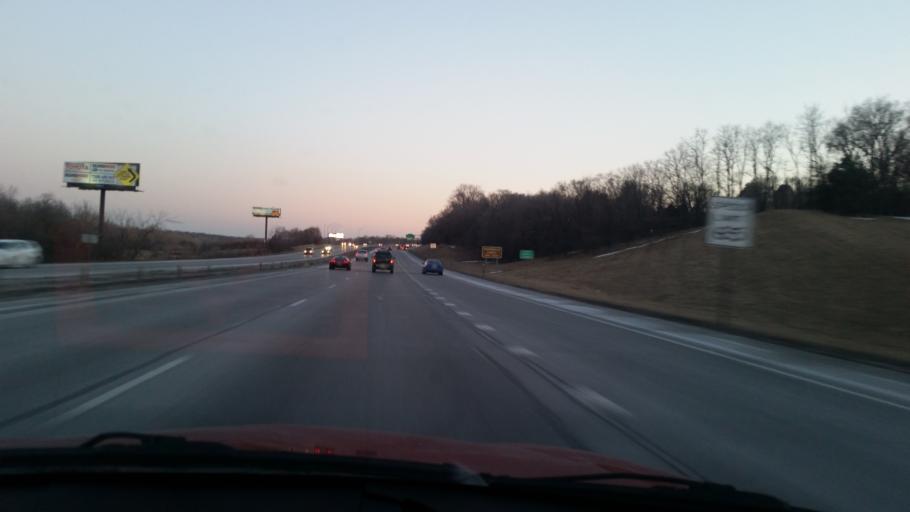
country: US
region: Nebraska
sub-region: Douglas County
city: Omaha
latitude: 41.1920
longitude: -95.9402
